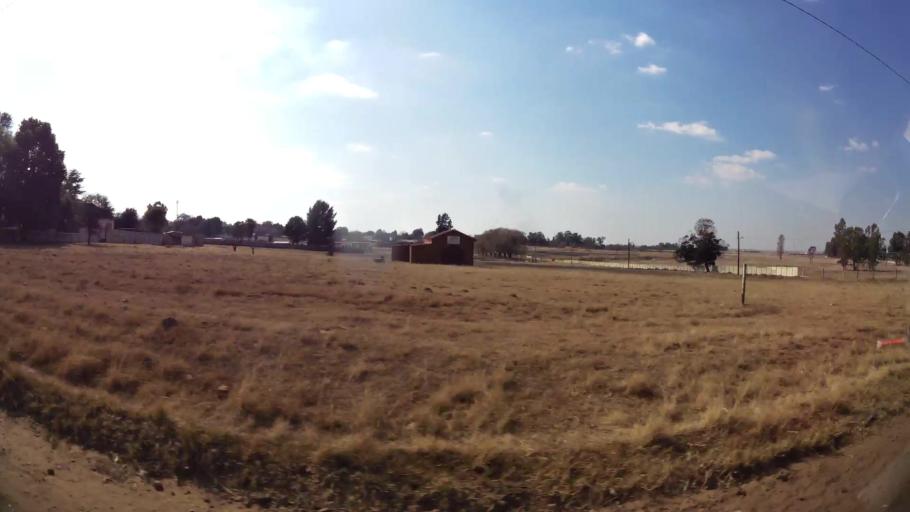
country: ZA
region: Gauteng
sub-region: Ekurhuleni Metropolitan Municipality
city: Benoni
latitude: -26.1112
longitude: 28.4017
